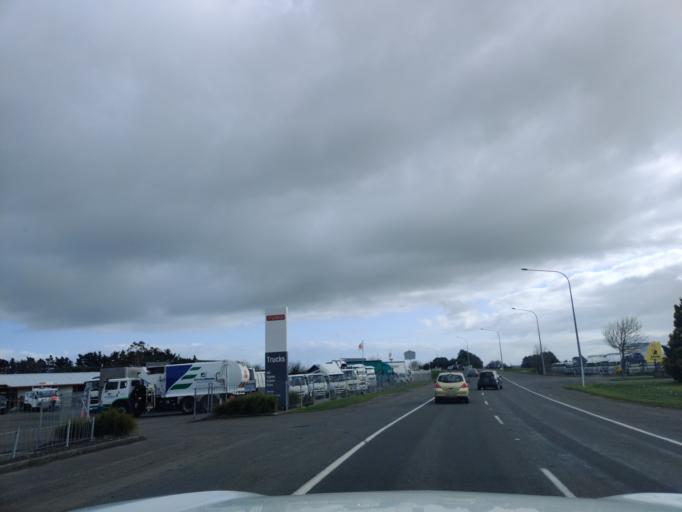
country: NZ
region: Manawatu-Wanganui
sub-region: Palmerston North City
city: Palmerston North
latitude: -40.3380
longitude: 175.5951
